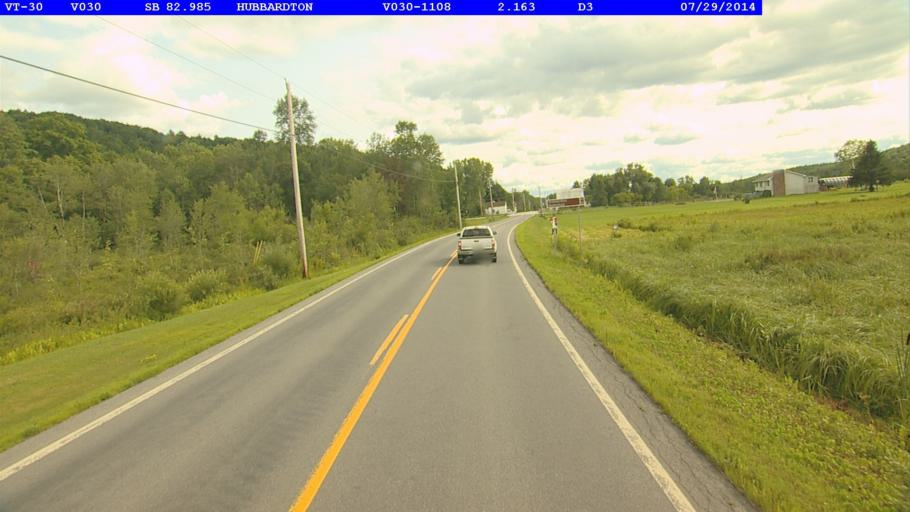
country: US
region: Vermont
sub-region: Rutland County
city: Castleton
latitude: 43.7091
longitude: -73.1845
